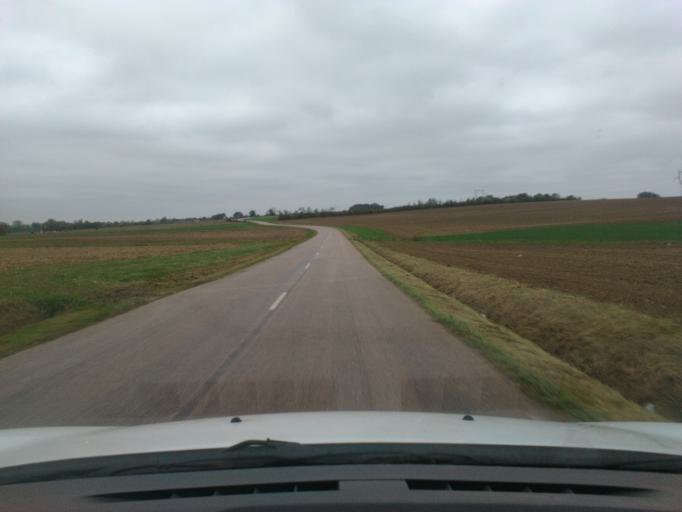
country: FR
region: Lorraine
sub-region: Departement des Vosges
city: Aydoilles
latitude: 48.2512
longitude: 6.5913
